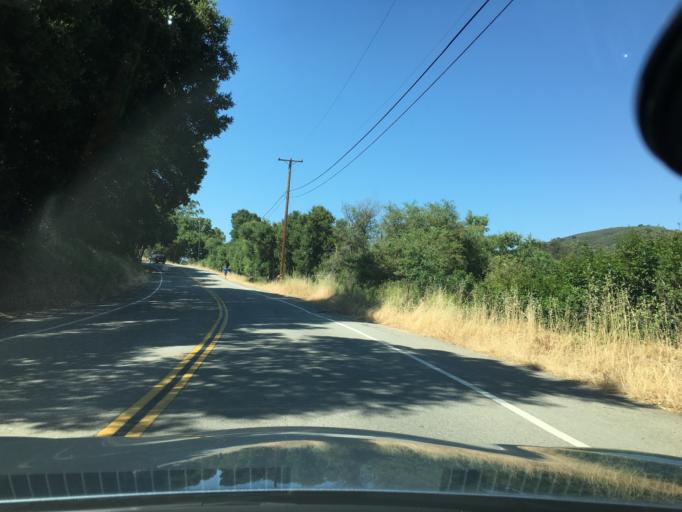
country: US
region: California
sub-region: Santa Clara County
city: Lexington Hills
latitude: 37.1793
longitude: -121.9892
